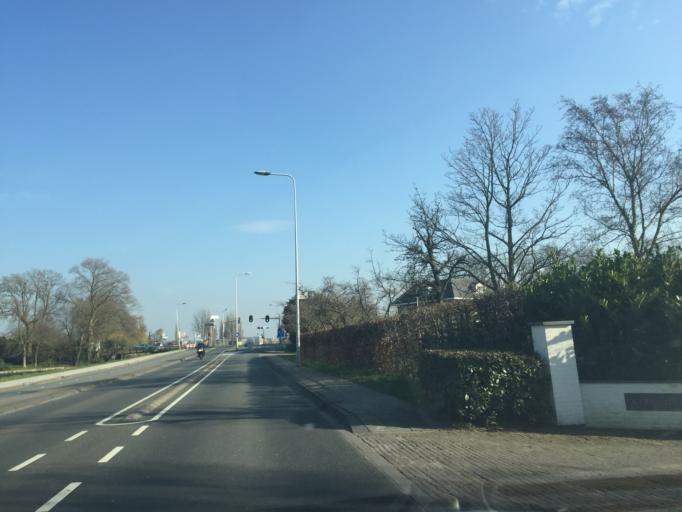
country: NL
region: South Holland
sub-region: Gemeente Oegstgeest
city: Oegstgeest
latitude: 52.1885
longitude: 4.4882
